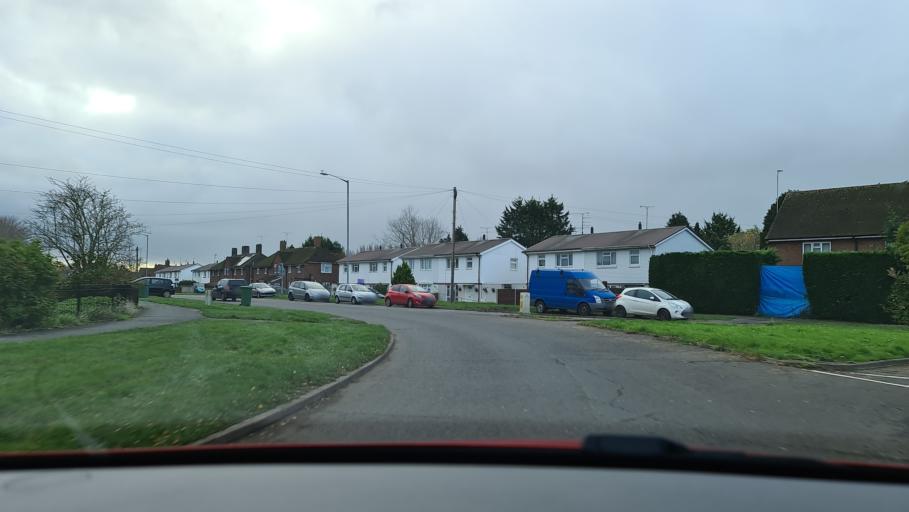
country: GB
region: England
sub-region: Buckinghamshire
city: Aylesbury
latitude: 51.8100
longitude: -0.8240
